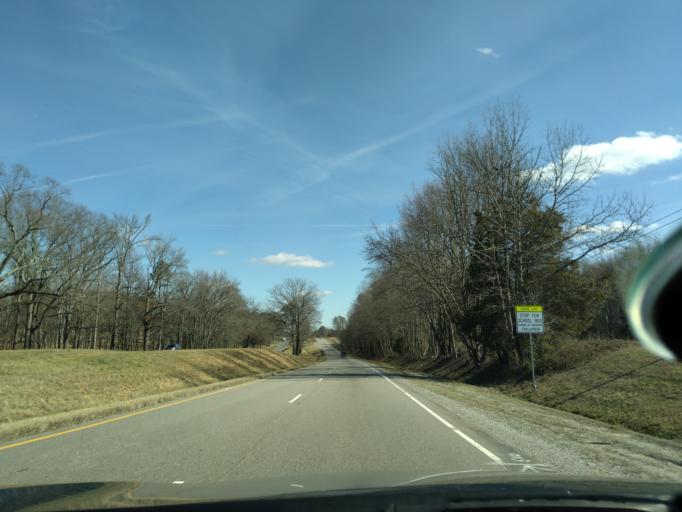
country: US
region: Virginia
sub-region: Nottoway County
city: Crewe
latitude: 37.1897
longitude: -78.1787
